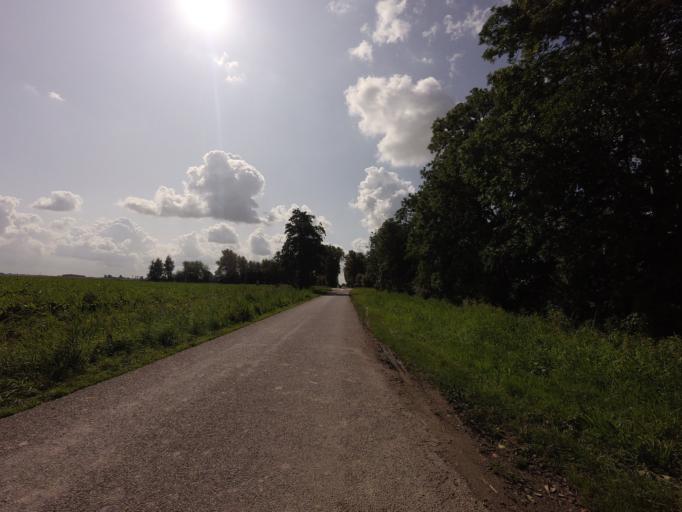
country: NL
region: Friesland
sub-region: Gemeente Het Bildt
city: Sint Annaparochie
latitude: 53.2790
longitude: 5.6757
